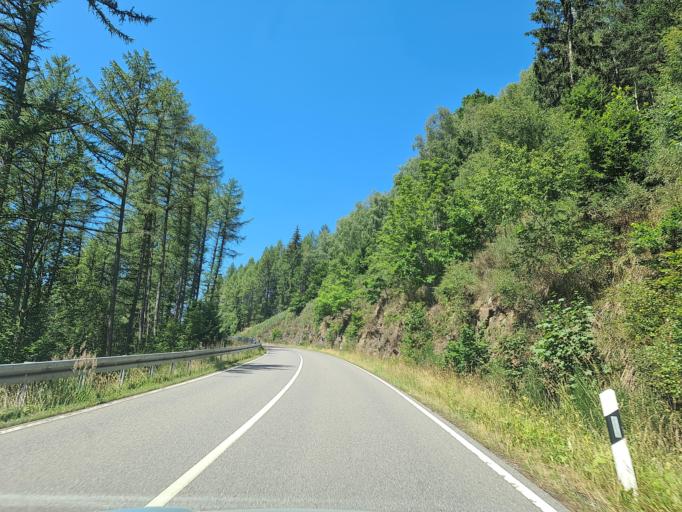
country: DE
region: Saxony
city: Neuhausen
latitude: 50.6911
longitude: 13.5055
